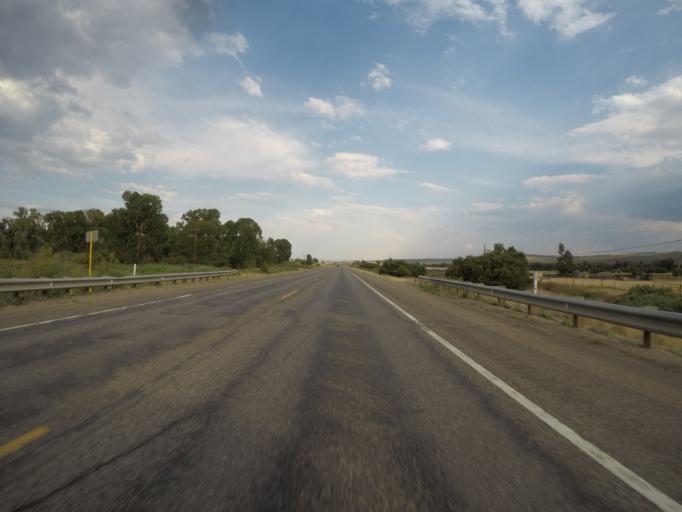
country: US
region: Colorado
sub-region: Moffat County
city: Craig
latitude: 40.5309
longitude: -107.4361
